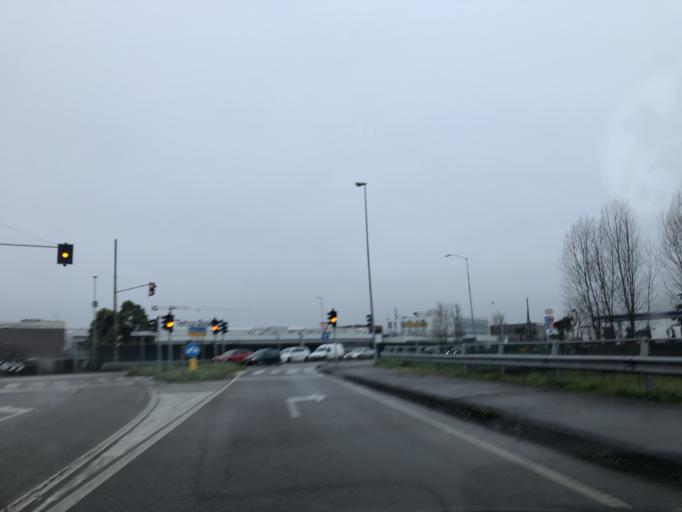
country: IT
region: Emilia-Romagna
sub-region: Provincia di Modena
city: Modena
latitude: 44.6574
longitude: 10.8829
